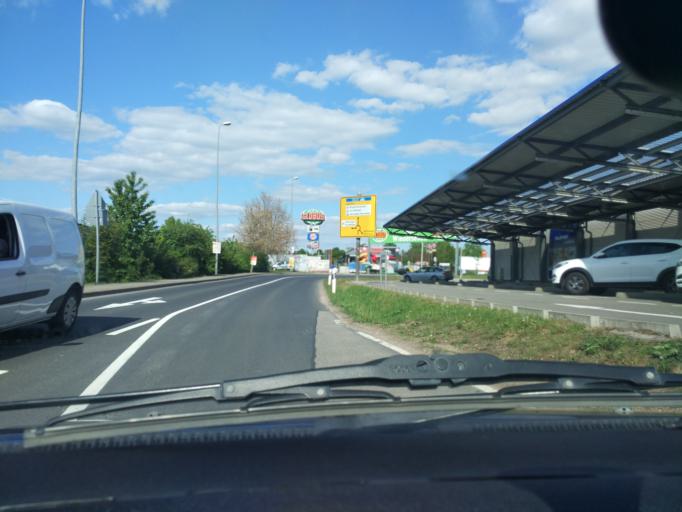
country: DE
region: Rheinland-Pfalz
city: Gensingen
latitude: 49.9010
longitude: 7.9283
